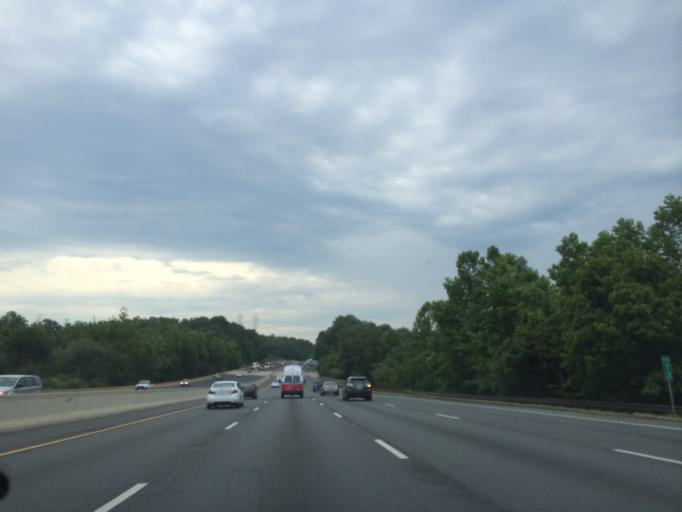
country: US
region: Maryland
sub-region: Montgomery County
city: Germantown
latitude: 39.1623
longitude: -77.2357
